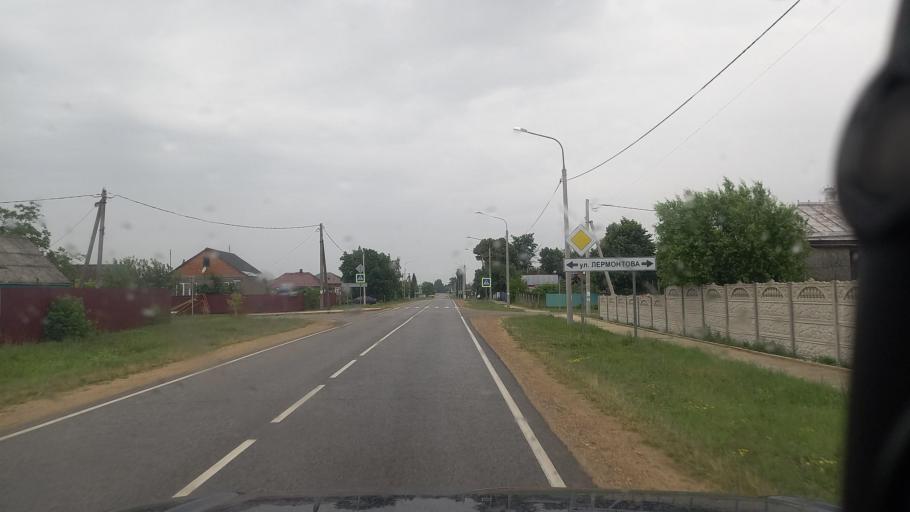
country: RU
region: Krasnodarskiy
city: Ryazanskaya
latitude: 44.9620
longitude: 39.5817
